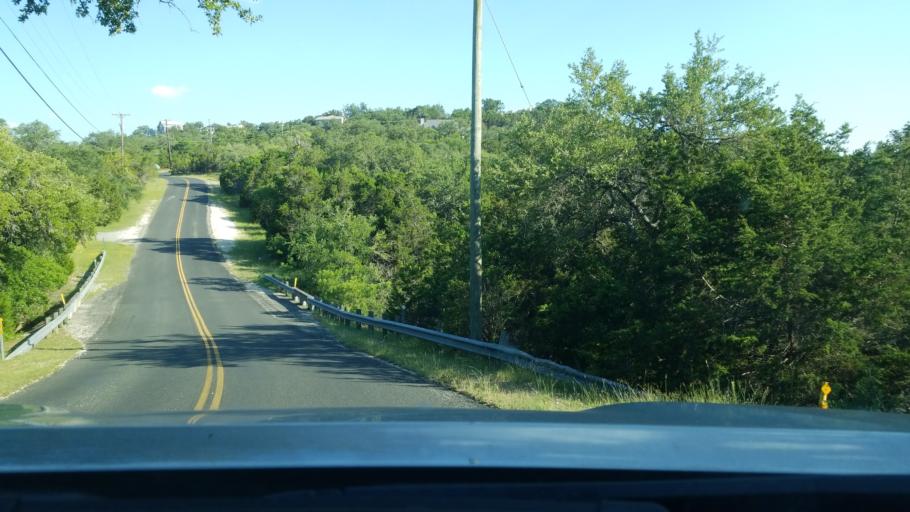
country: US
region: Texas
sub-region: Comal County
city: Bulverde
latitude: 29.7125
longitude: -98.4461
